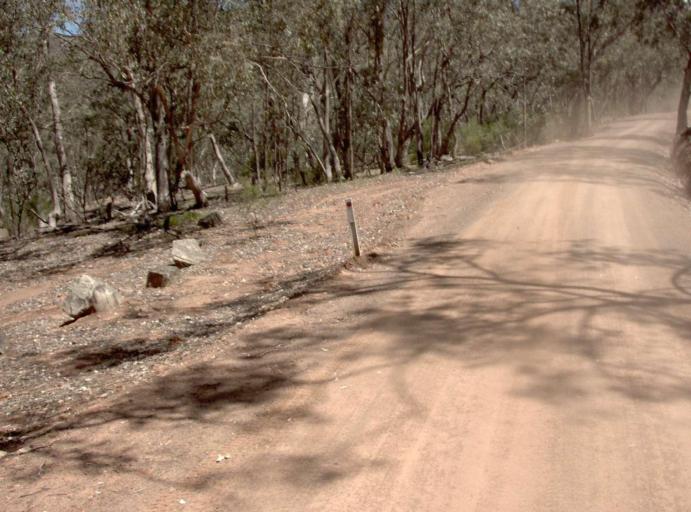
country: AU
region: New South Wales
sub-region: Snowy River
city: Jindabyne
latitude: -37.0887
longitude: 148.4130
